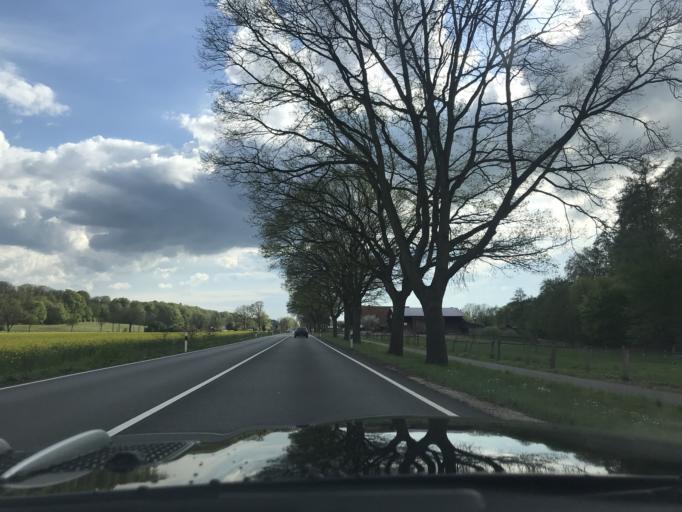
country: DE
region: Schleswig-Holstein
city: Fredeburg
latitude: 53.6535
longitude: 10.7110
